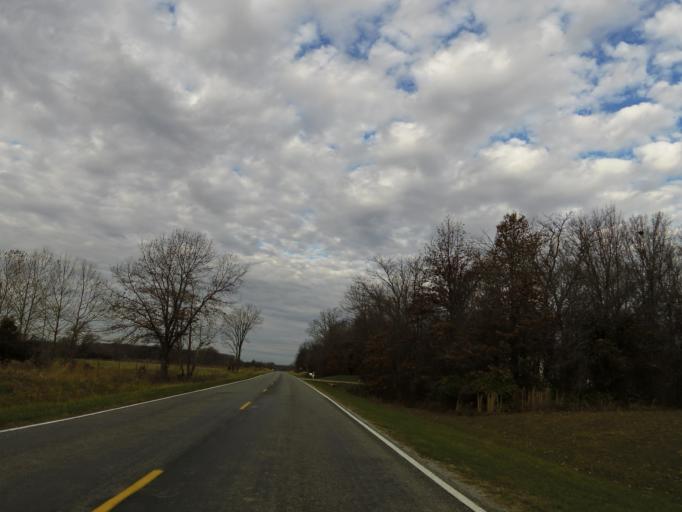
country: US
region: Illinois
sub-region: Jefferson County
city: Mount Vernon
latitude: 38.3636
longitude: -88.9798
